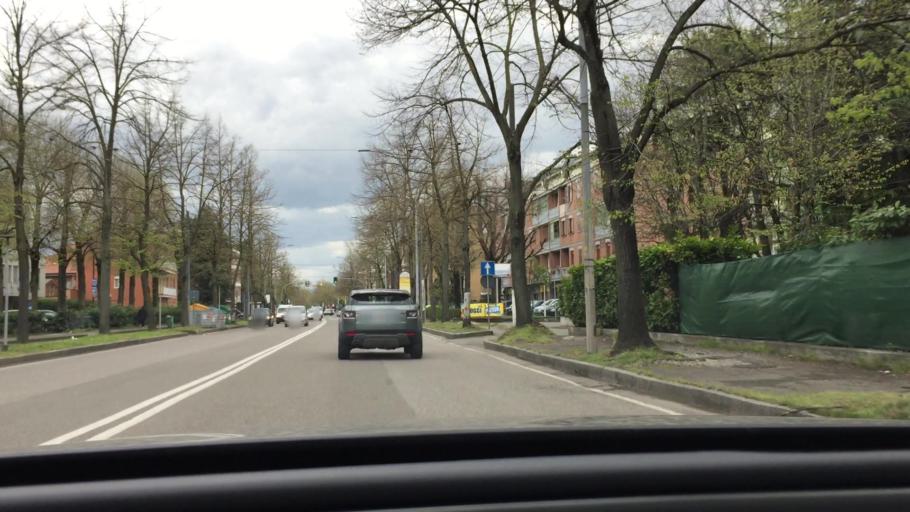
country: IT
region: Emilia-Romagna
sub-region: Provincia di Modena
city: Modena
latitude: 44.6328
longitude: 10.9013
